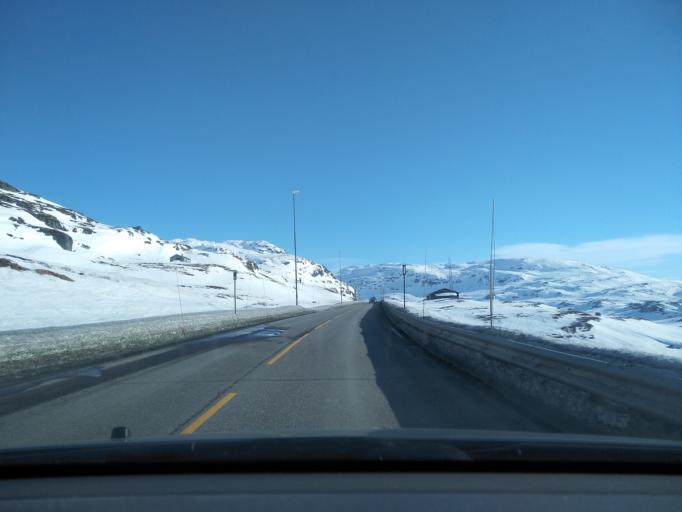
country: NO
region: Aust-Agder
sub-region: Bykle
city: Hovden
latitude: 59.8418
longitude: 6.9795
